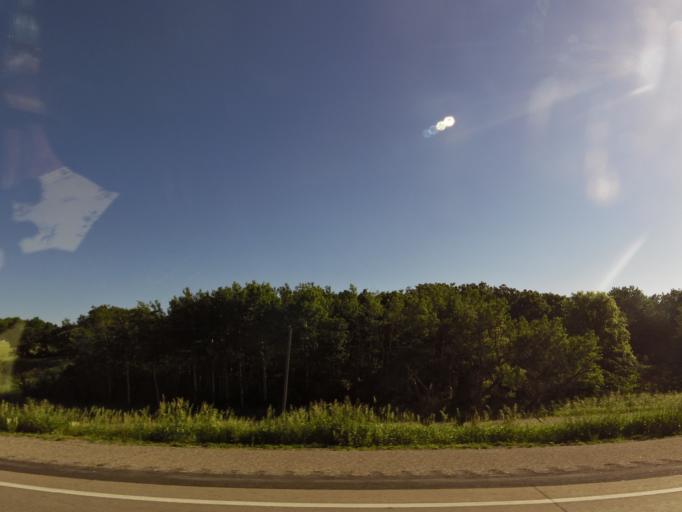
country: US
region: Minnesota
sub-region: Stearns County
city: Sauk Centre
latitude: 45.7579
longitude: -95.0139
